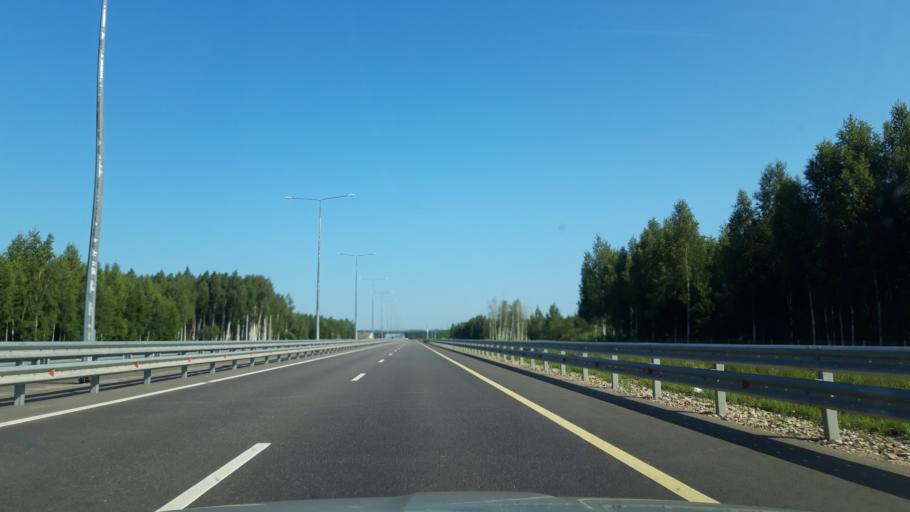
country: RU
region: Tverskaya
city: Zavidovo
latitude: 56.5417
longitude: 36.4928
